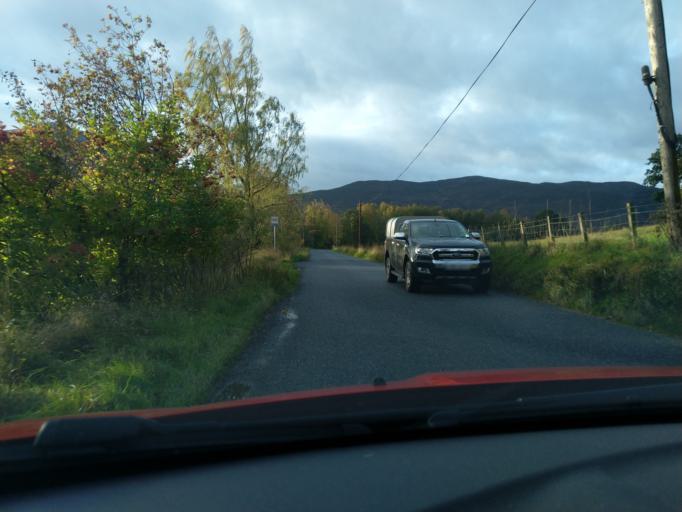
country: GB
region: Scotland
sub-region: Perth and Kinross
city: Aberfeldy
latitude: 56.7030
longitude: -4.1345
